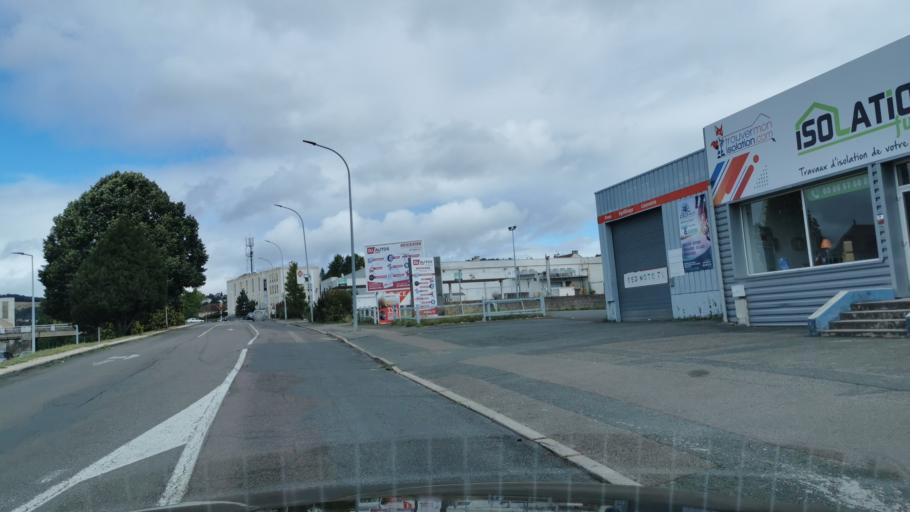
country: FR
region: Bourgogne
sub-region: Departement de Saone-et-Loire
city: Le Creusot
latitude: 46.7981
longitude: 4.4408
